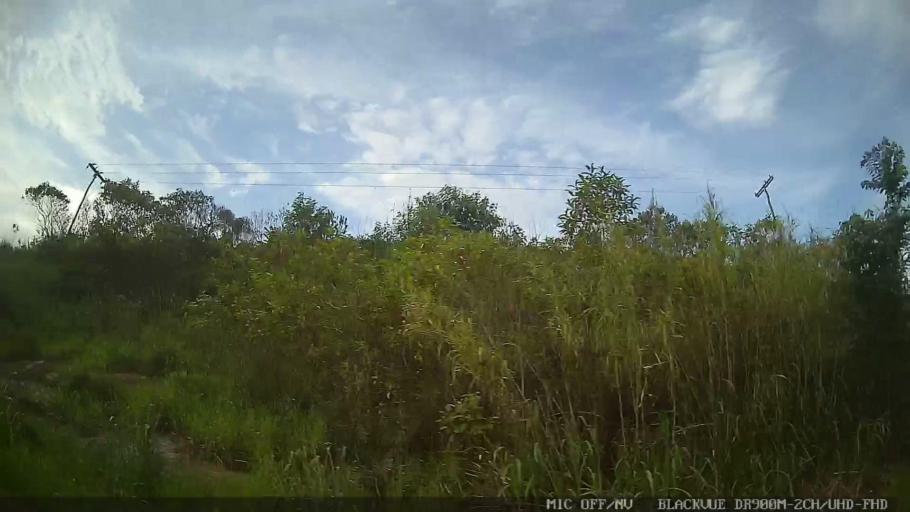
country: BR
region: Sao Paulo
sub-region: Amparo
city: Amparo
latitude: -22.6922
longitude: -46.7271
